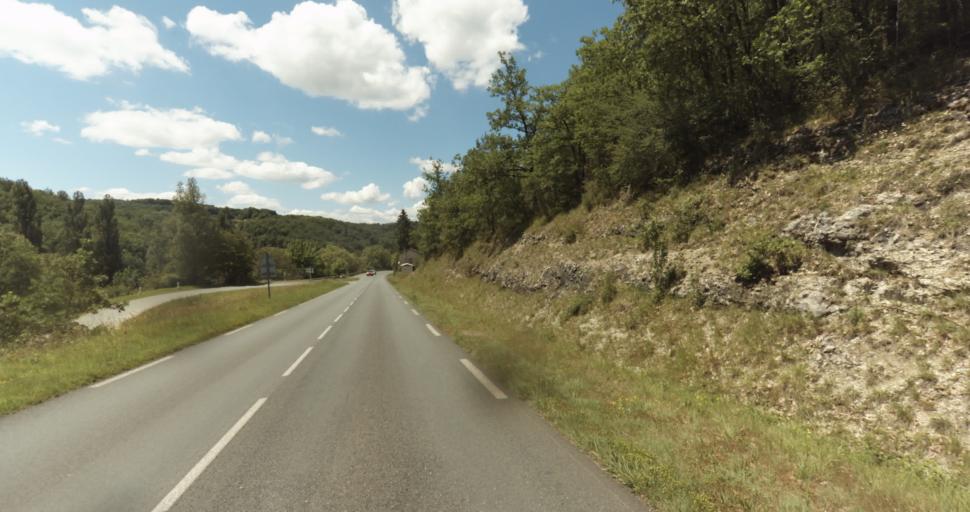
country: FR
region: Aquitaine
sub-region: Departement de la Dordogne
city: Lalinde
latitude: 44.8465
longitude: 0.8215
